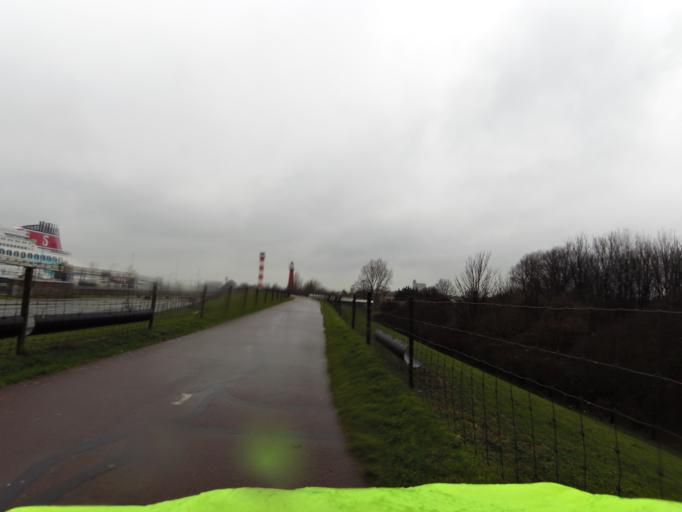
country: NL
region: South Holland
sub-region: Gemeente Rotterdam
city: Hoek van Holland
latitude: 51.9732
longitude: 4.1362
